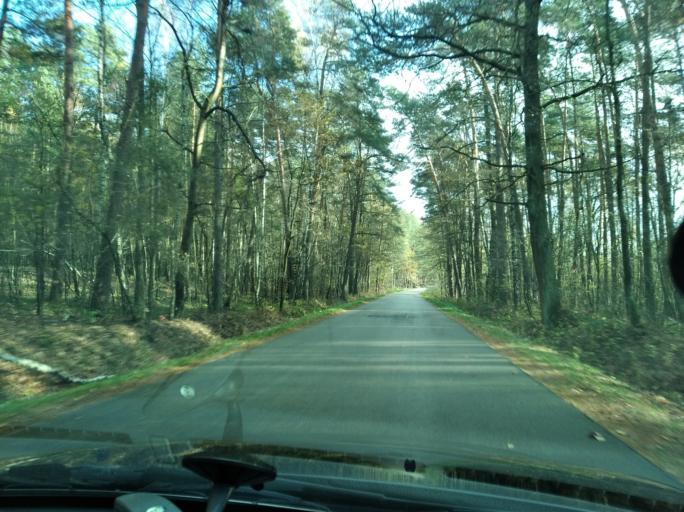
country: PL
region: Subcarpathian Voivodeship
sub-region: Powiat ropczycko-sedziszowski
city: Sedziszow Malopolski
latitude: 50.1207
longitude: 21.7176
